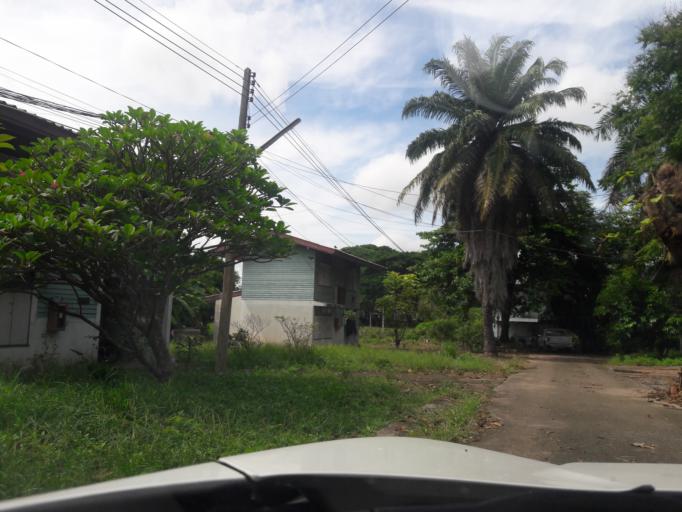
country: TH
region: Nakhon Sawan
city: Tak Fa
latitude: 15.3468
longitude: 100.4917
